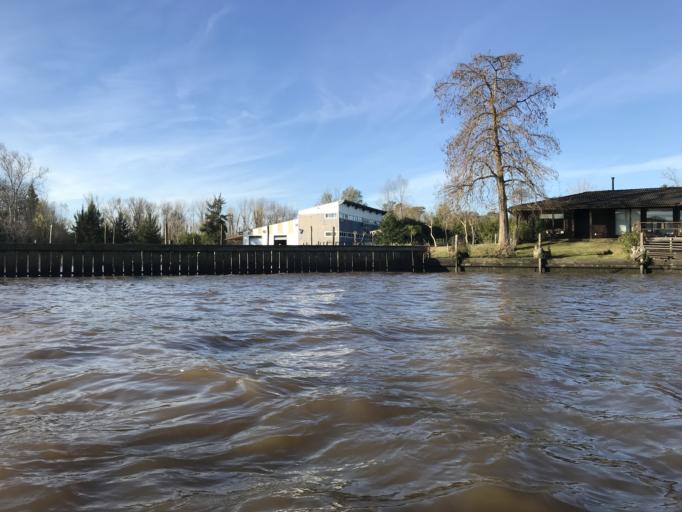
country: AR
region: Buenos Aires
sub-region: Partido de Tigre
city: Tigre
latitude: -34.4058
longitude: -58.5927
